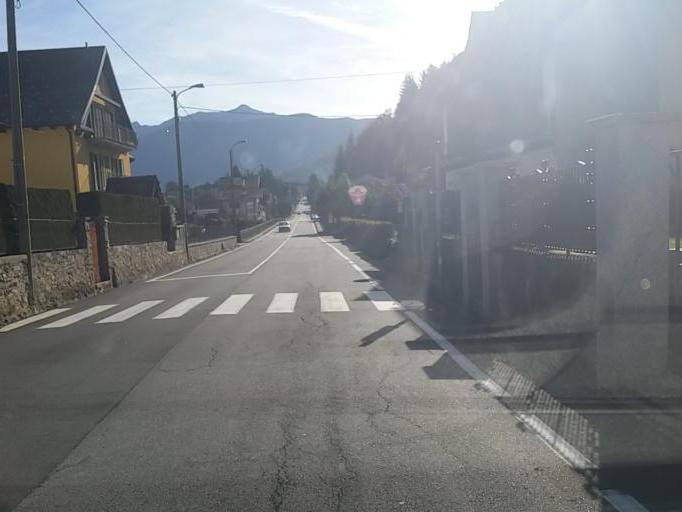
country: IT
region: Piedmont
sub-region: Provincia Verbano-Cusio-Ossola
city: Malesco
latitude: 46.1293
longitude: 8.4914
